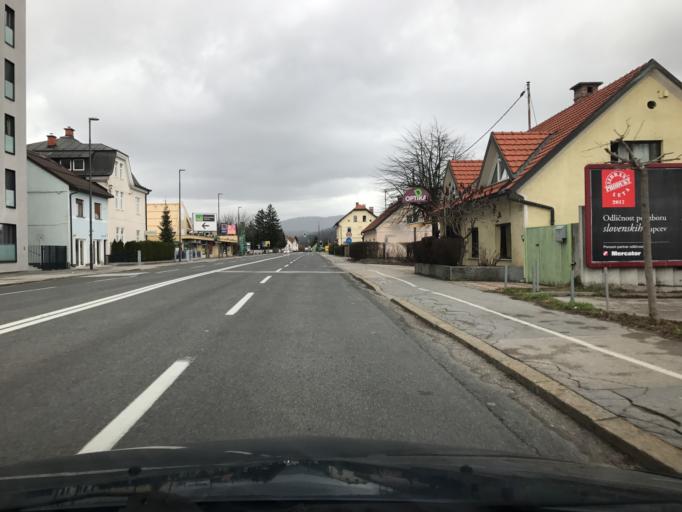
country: SI
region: Ljubljana
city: Ljubljana
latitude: 46.0876
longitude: 14.5140
